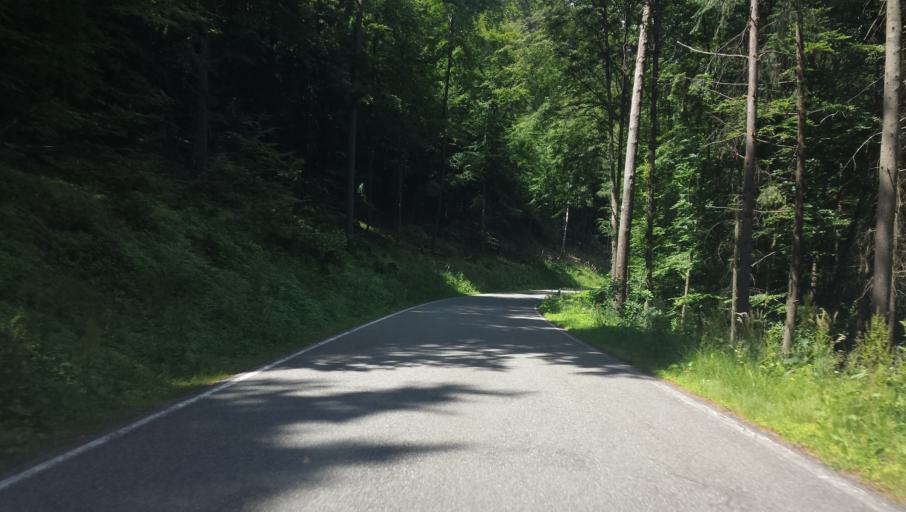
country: DE
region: Rheinland-Pfalz
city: Wernersberg
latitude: 49.1869
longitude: 7.9544
